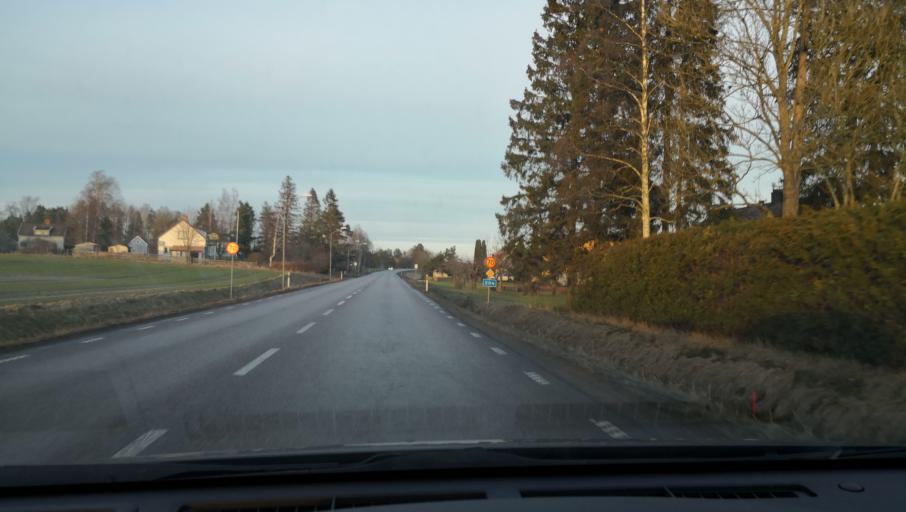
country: SE
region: OErebro
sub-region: Lekebergs Kommun
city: Fjugesta
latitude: 59.1638
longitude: 14.8302
